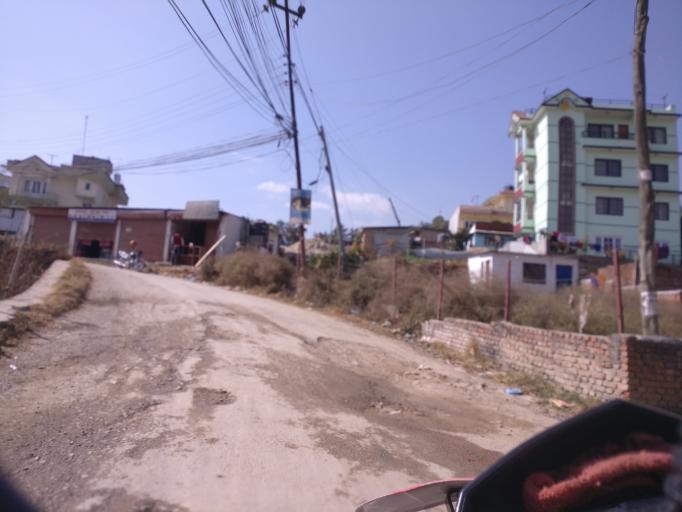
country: NP
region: Central Region
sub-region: Bagmati Zone
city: Patan
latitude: 27.6488
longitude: 85.3095
